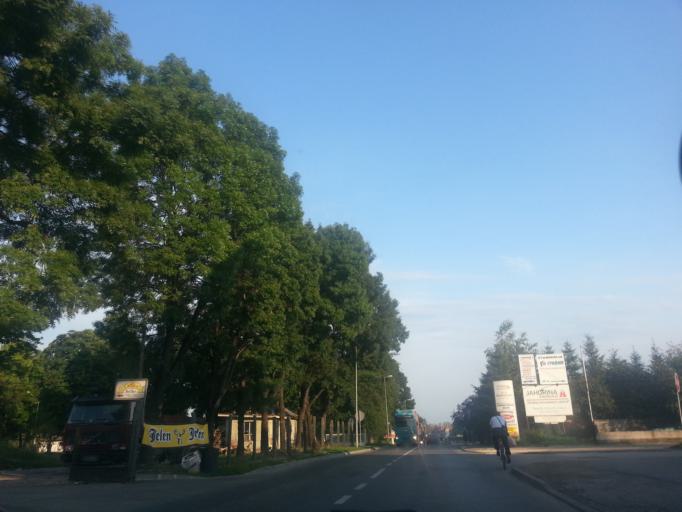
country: BA
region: Brcko
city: Brcko
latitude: 44.8673
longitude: 18.8196
